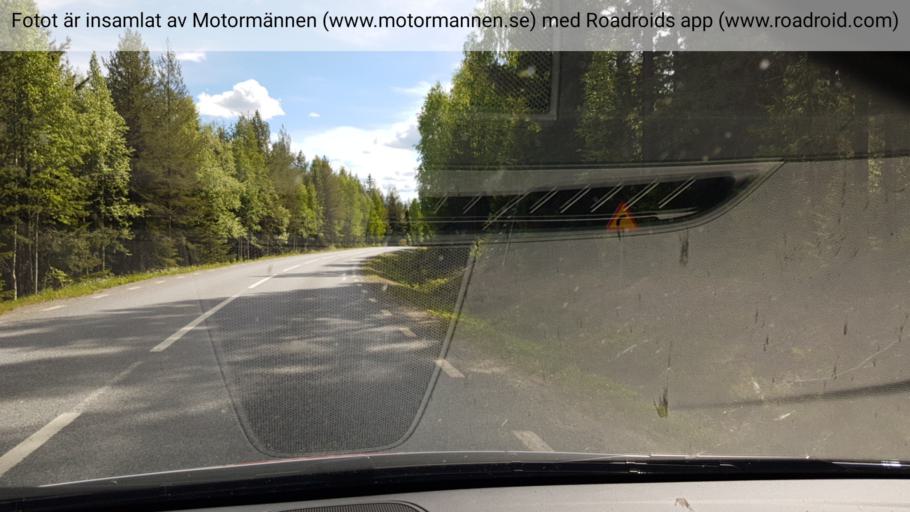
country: SE
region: Vaesterbotten
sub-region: Skelleftea Kommun
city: Burtraesk
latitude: 64.4353
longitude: 20.3995
